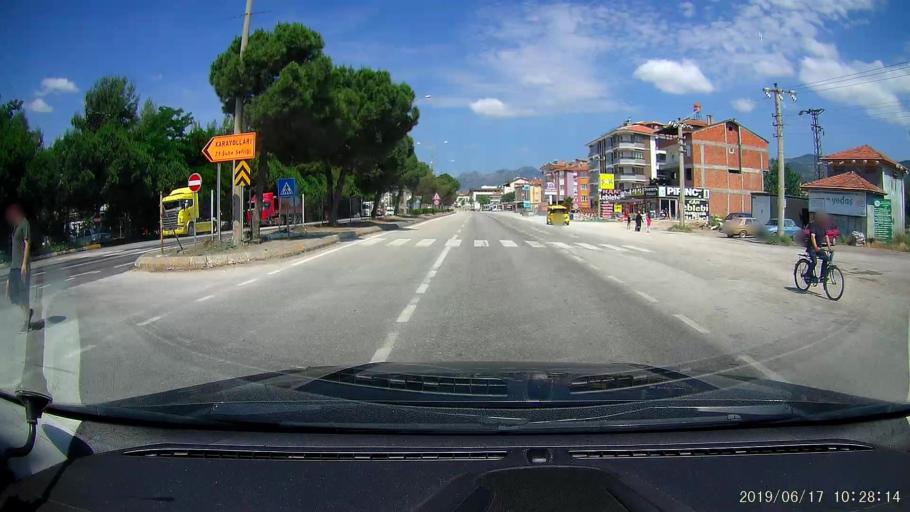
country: TR
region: Corum
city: Osmancik
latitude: 40.9771
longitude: 34.8106
